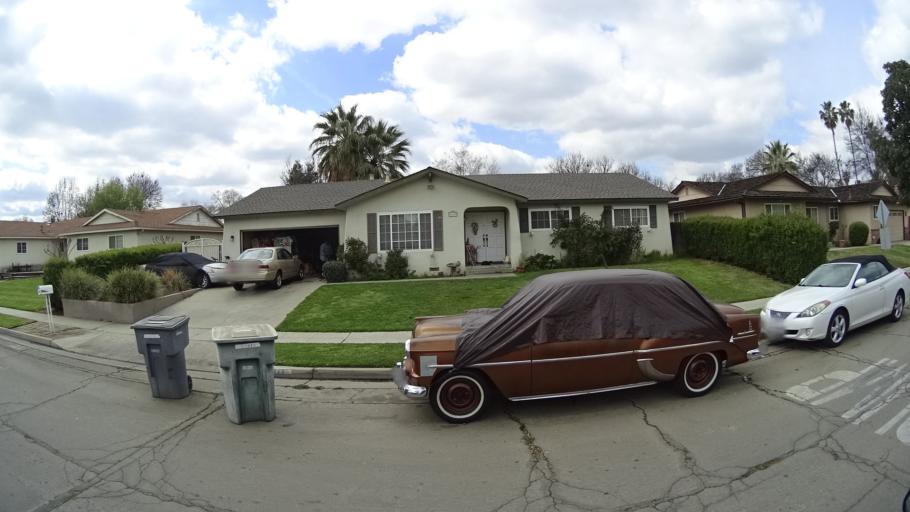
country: US
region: California
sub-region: Fresno County
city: Fresno
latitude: 36.8313
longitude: -119.8235
